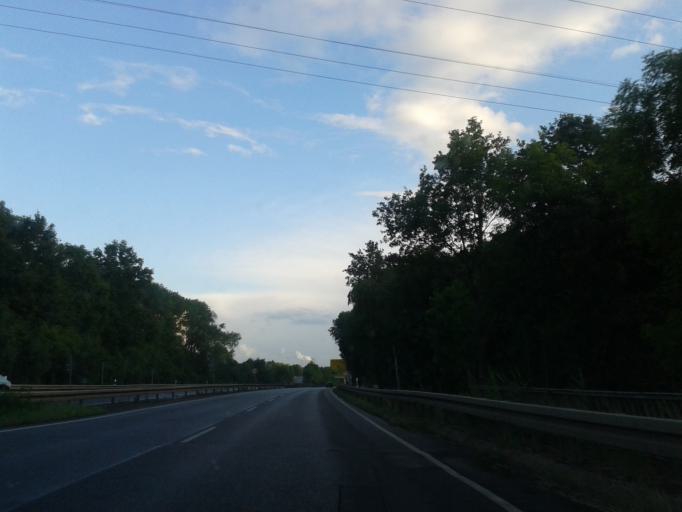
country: DE
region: Saxony
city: Markkleeberg
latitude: 51.2777
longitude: 12.3834
